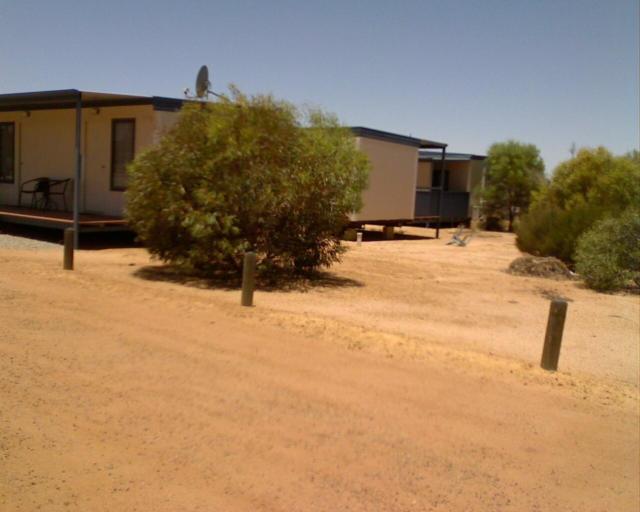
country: AU
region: Western Australia
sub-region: Merredin
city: Merredin
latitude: -30.8187
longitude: 117.8631
